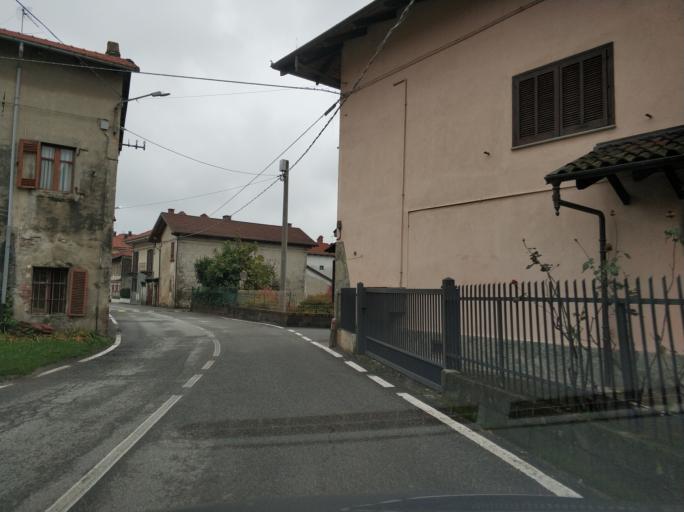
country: IT
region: Piedmont
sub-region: Provincia di Torino
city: Villanova Canavese
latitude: 45.2440
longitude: 7.5477
